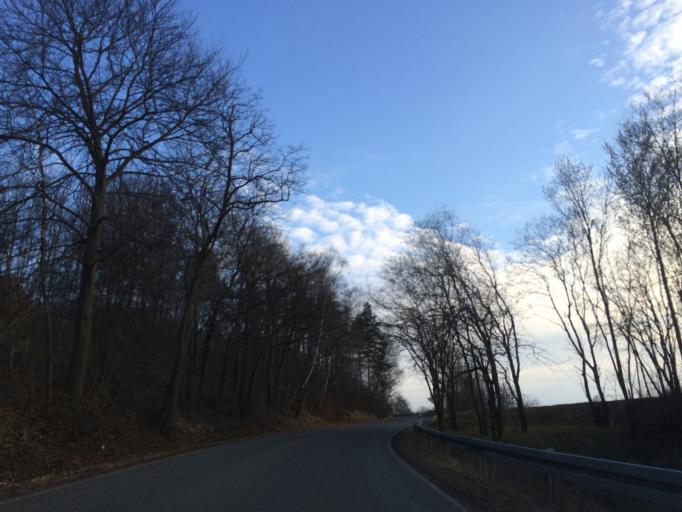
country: DE
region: Thuringia
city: Konitz
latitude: 50.6451
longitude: 11.4924
